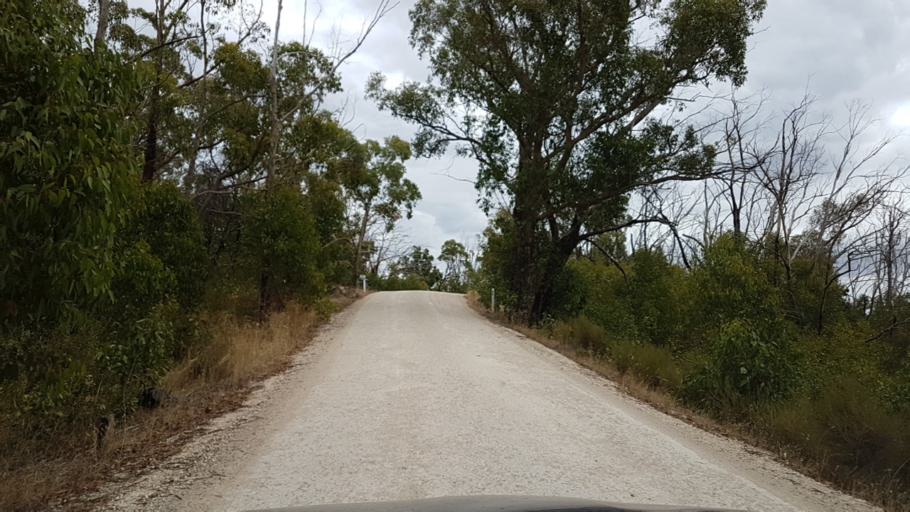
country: AU
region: South Australia
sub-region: Tea Tree Gully
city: Golden Grove
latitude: -34.7806
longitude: 138.8136
